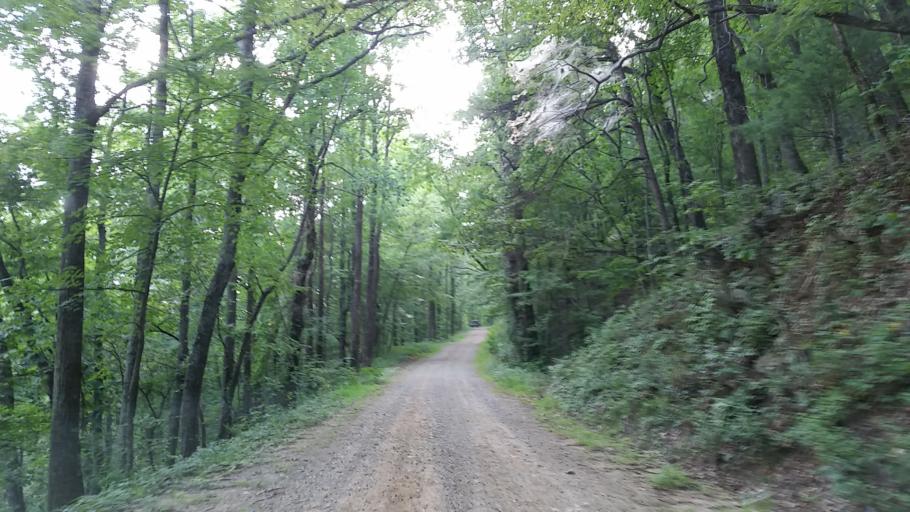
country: US
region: Georgia
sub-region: Lumpkin County
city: Dahlonega
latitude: 34.6488
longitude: -84.0750
